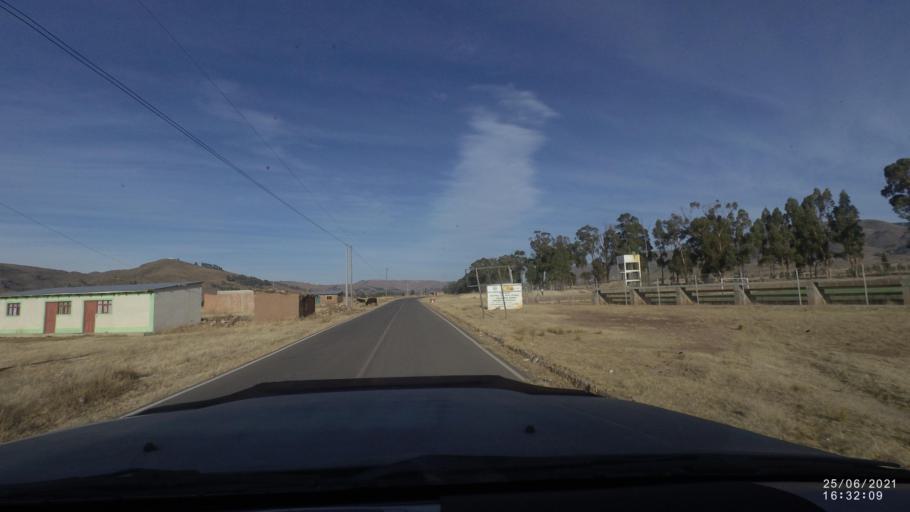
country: BO
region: Cochabamba
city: Arani
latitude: -17.8049
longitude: -65.7979
